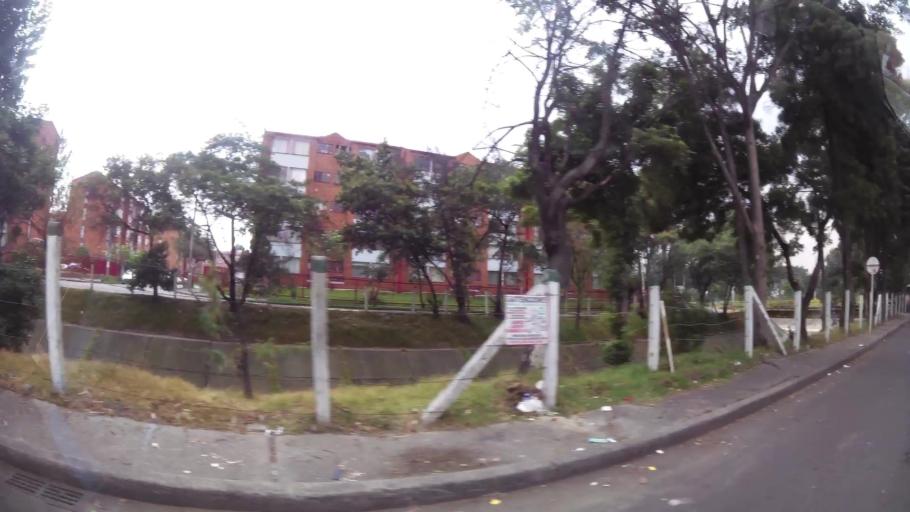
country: CO
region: Bogota D.C.
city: Bogota
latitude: 4.6008
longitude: -74.1166
